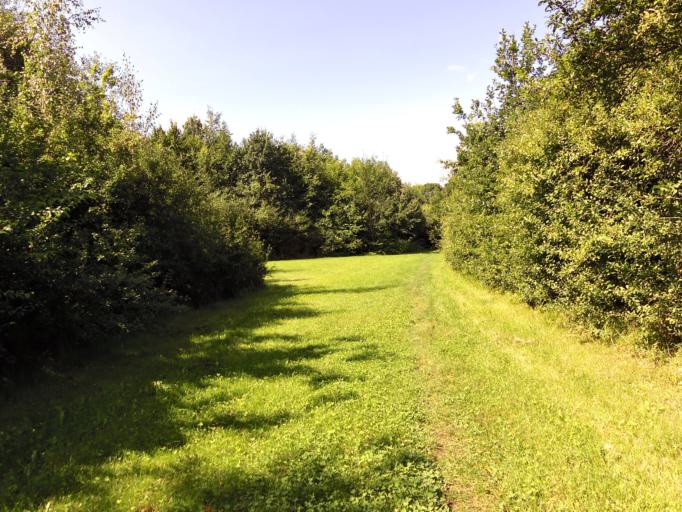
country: DE
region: Saxony
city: Markkleeberg
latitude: 51.3045
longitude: 12.4089
